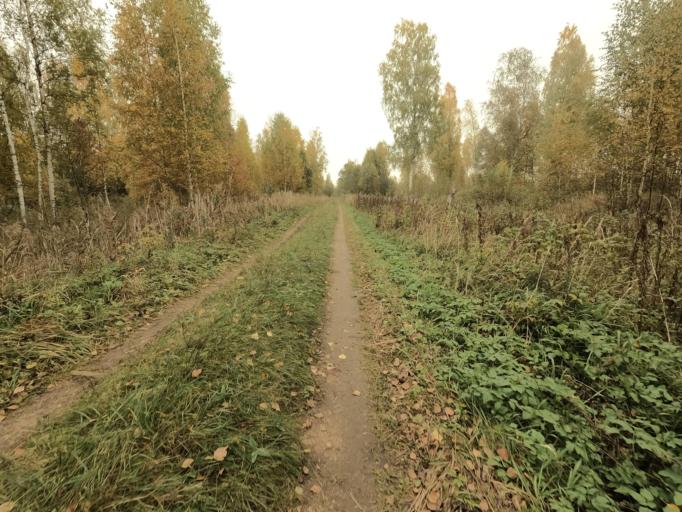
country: RU
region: Novgorod
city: Pankovka
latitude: 58.8681
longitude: 30.9350
